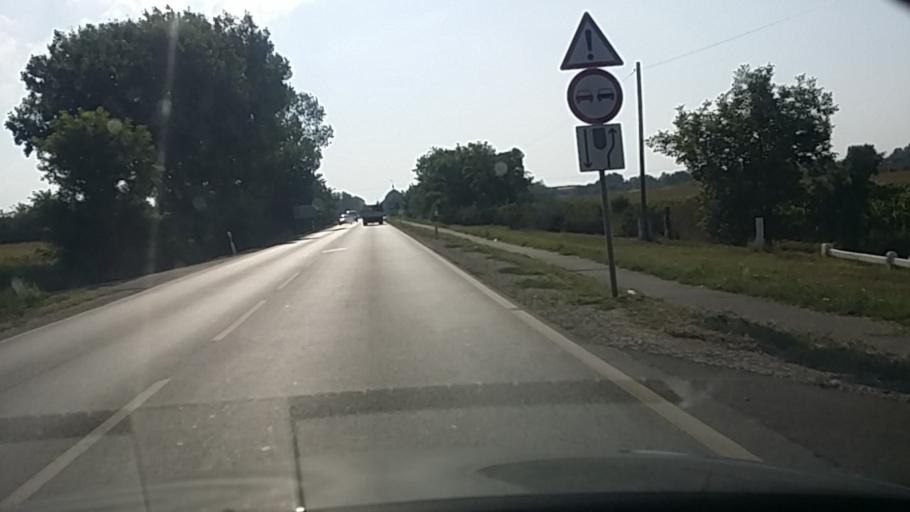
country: HU
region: Bekes
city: Kondoros
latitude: 46.7634
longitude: 20.7824
